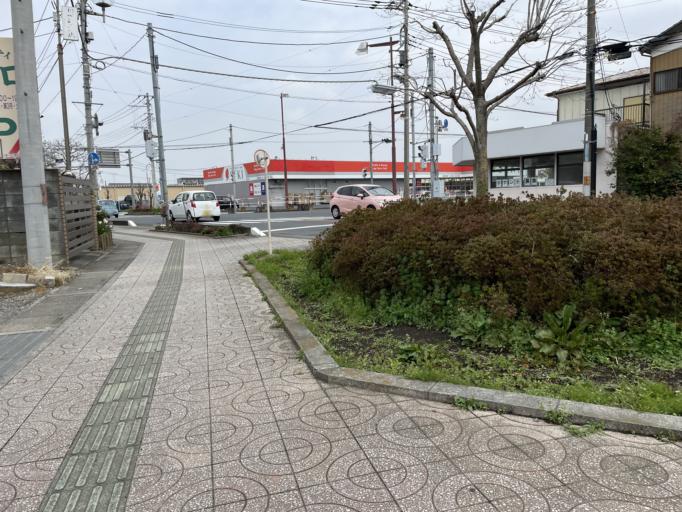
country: JP
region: Saitama
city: Hanyu
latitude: 36.1674
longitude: 139.5394
